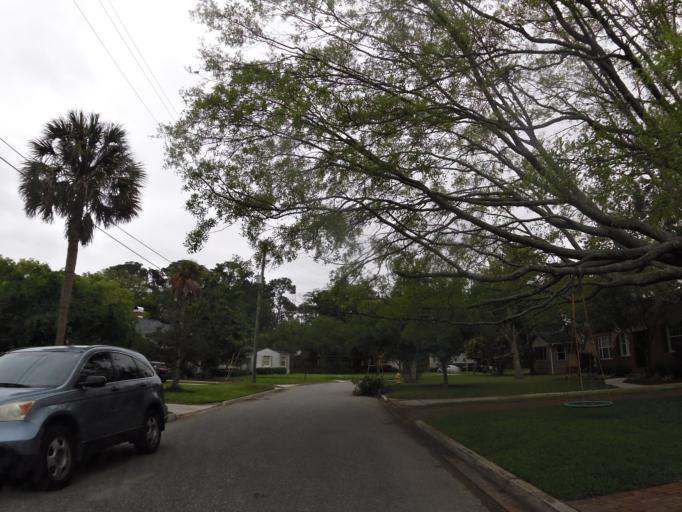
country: US
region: Florida
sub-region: Duval County
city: Jacksonville
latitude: 30.2933
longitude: -81.6469
